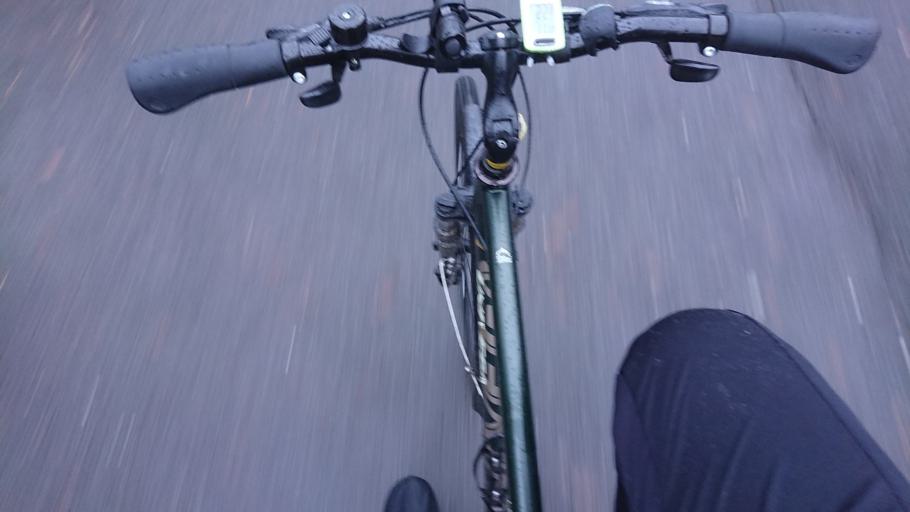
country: FI
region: Pirkanmaa
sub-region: Tampere
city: Tampere
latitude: 61.4612
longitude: 23.8739
